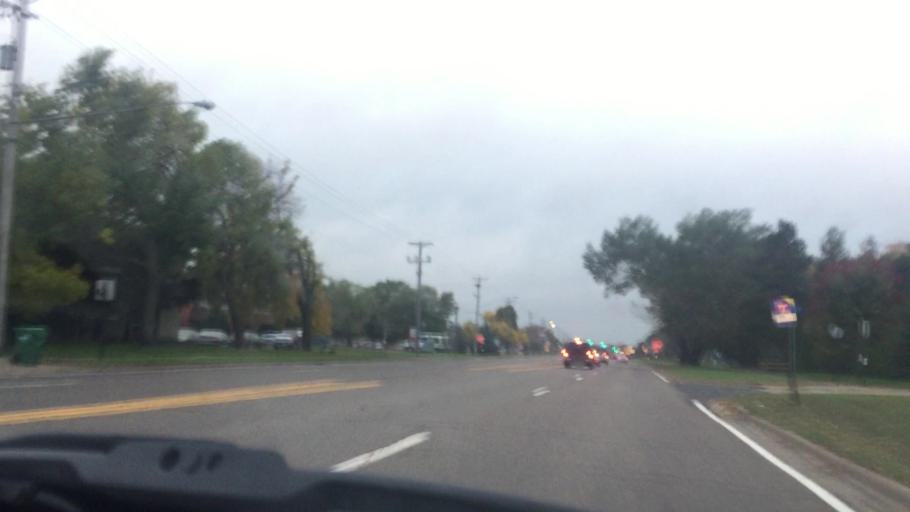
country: US
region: Minnesota
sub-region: Anoka County
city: Spring Lake Park
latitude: 45.1079
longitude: -93.2519
